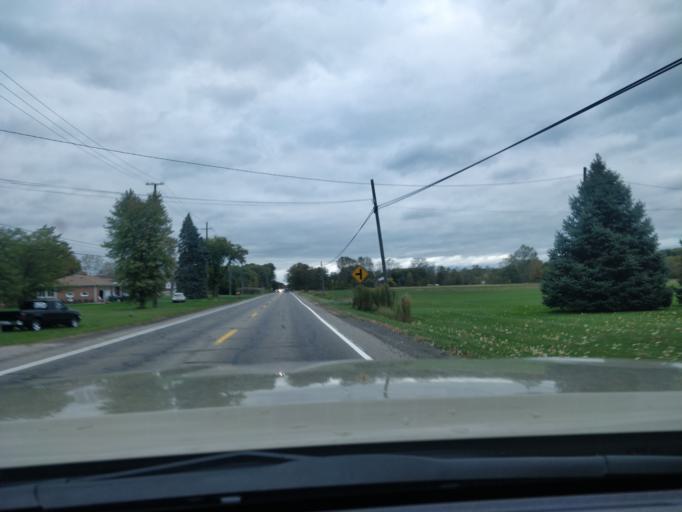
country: US
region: Michigan
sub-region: Wayne County
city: Romulus
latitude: 42.1808
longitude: -83.3362
